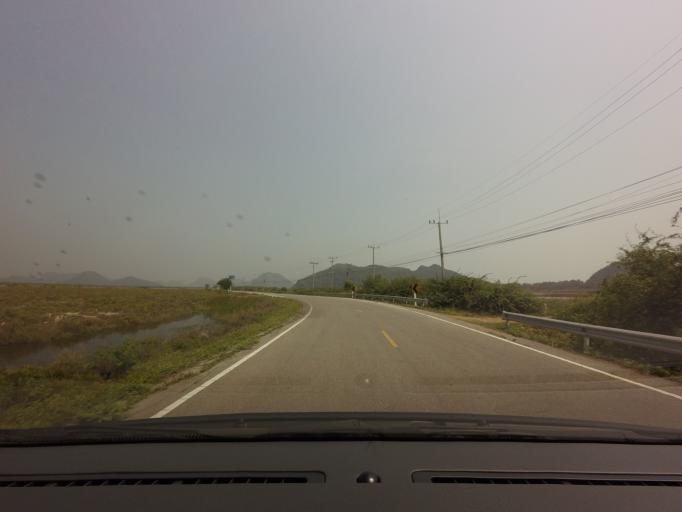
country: TH
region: Prachuap Khiri Khan
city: Kui Buri
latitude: 12.1534
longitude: 99.9749
